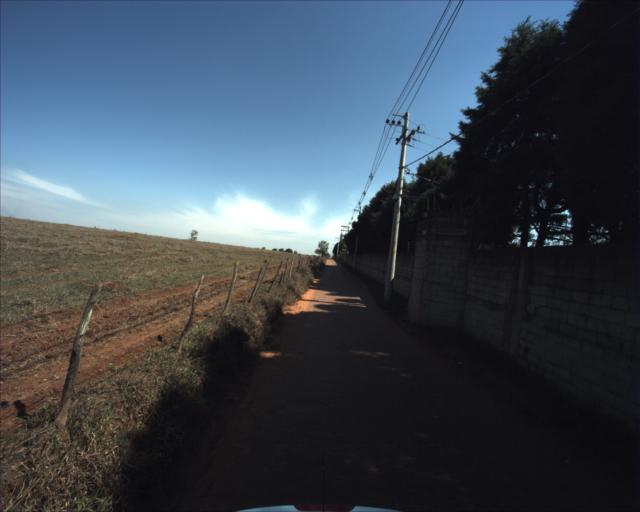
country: BR
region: Sao Paulo
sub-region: Aracoiaba Da Serra
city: Aracoiaba da Serra
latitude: -23.4843
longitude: -47.5404
